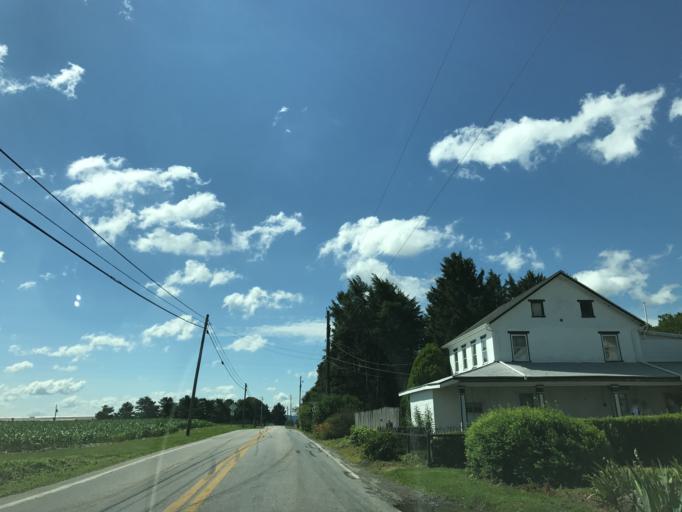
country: US
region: Pennsylvania
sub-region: Lancaster County
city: Rheems
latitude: 40.1159
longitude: -76.5940
